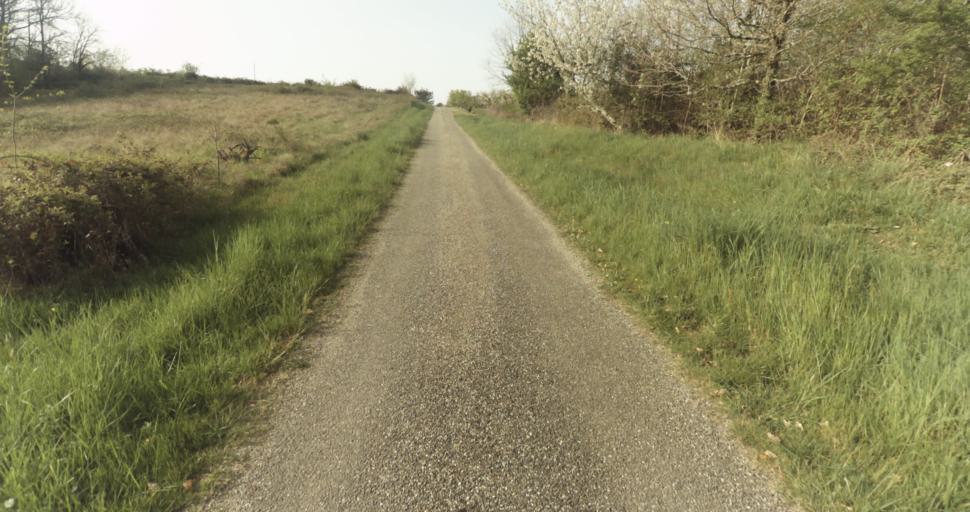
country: FR
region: Midi-Pyrenees
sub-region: Departement du Tarn-et-Garonne
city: Moissac
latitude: 44.1609
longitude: 1.0985
